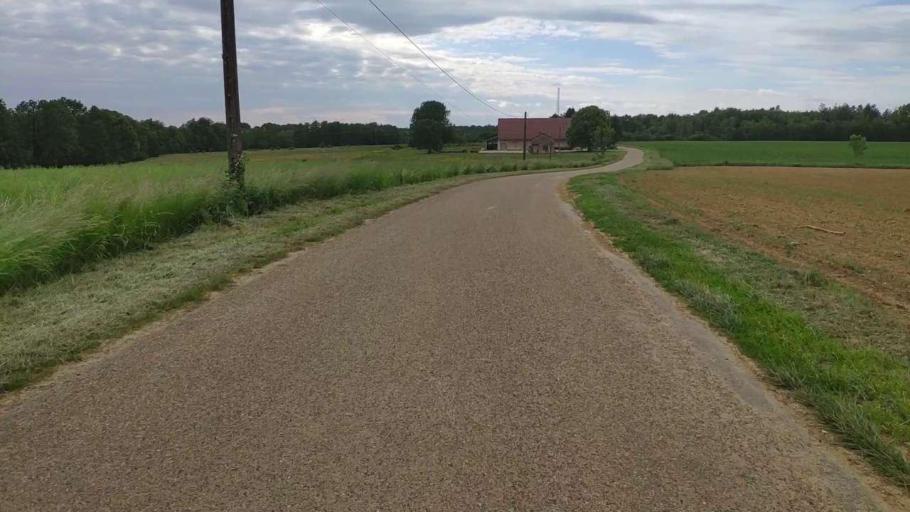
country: FR
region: Franche-Comte
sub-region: Departement du Jura
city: Bletterans
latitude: 46.8002
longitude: 5.5393
